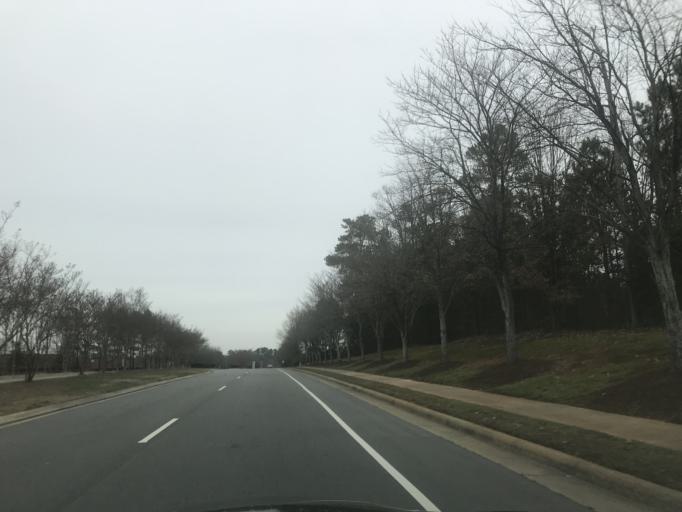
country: US
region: North Carolina
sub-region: Wake County
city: Raleigh
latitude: 35.8704
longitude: -78.5899
